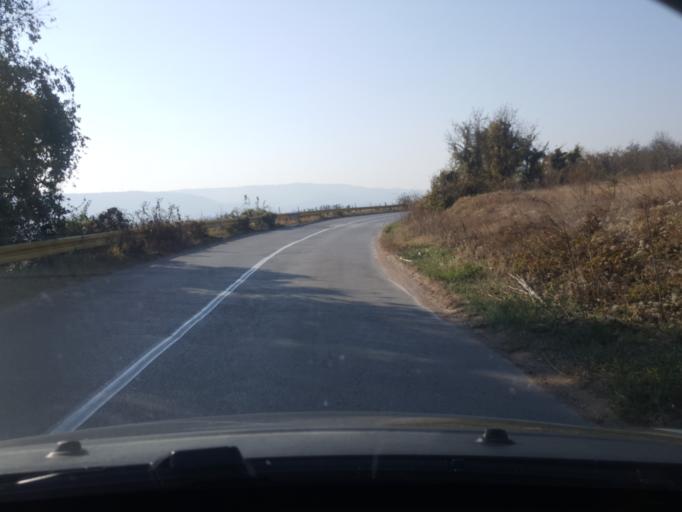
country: RS
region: Central Serbia
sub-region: Nisavski Okrug
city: Niska Banja
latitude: 43.3191
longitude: 22.0001
